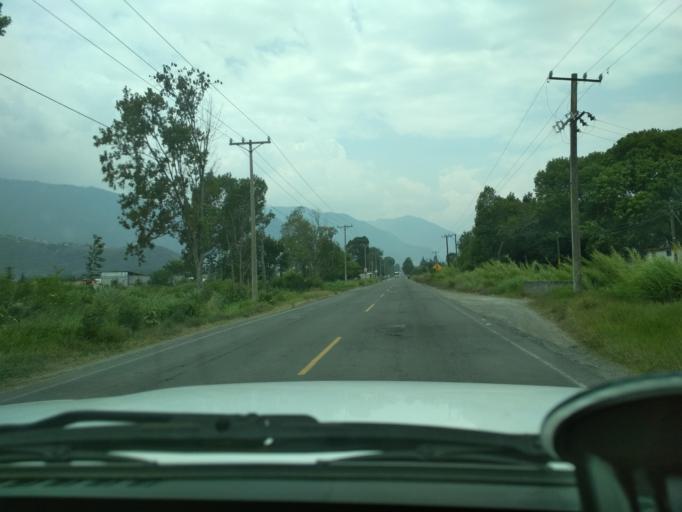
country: MX
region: Veracruz
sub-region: Nogales
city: Taza de Agua Ojo Zarco
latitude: 18.7742
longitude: -97.2134
